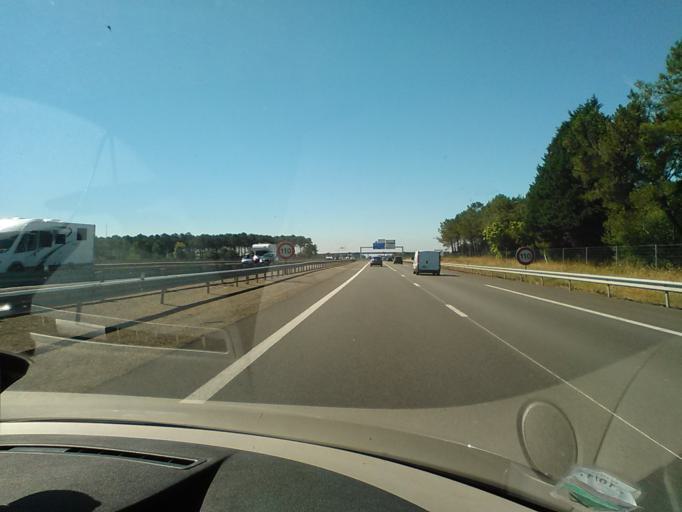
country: FR
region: Aquitaine
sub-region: Departement des Landes
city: Saint-Geours-de-Maremne
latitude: 43.7172
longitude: -1.2278
